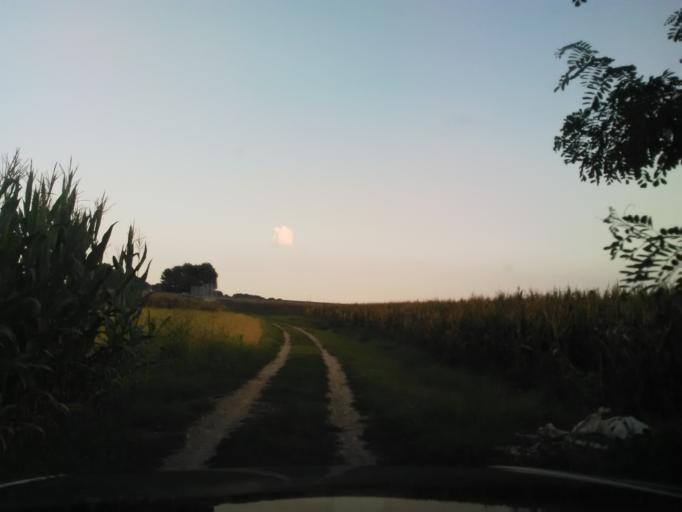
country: IT
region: Piedmont
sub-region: Provincia di Vercelli
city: Cigliano
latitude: 45.3077
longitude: 8.0389
